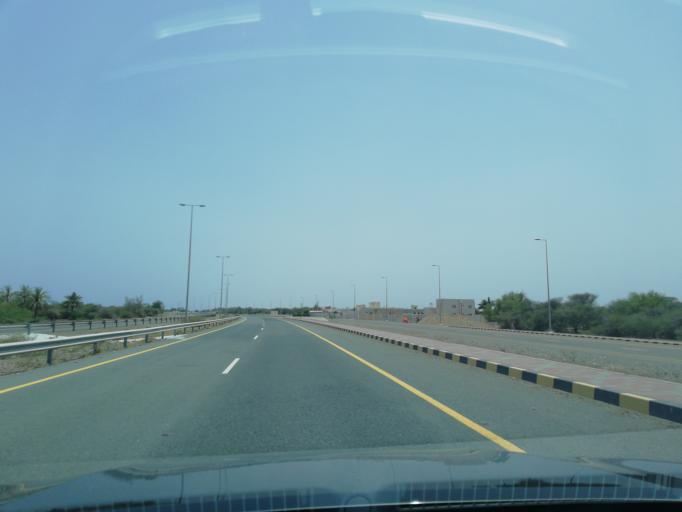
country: OM
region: Al Batinah
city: Shinas
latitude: 24.7941
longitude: 56.4523
